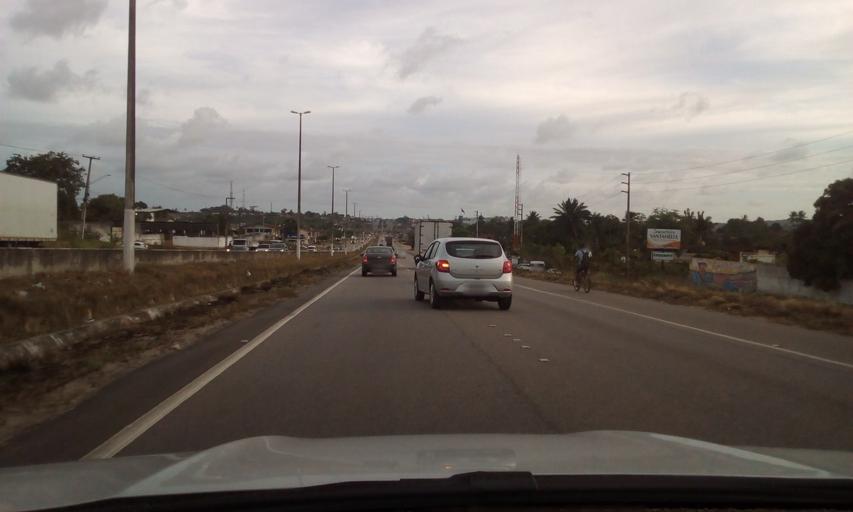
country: BR
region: Pernambuco
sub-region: Igarassu
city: Igarassu
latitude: -7.8224
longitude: -34.9163
